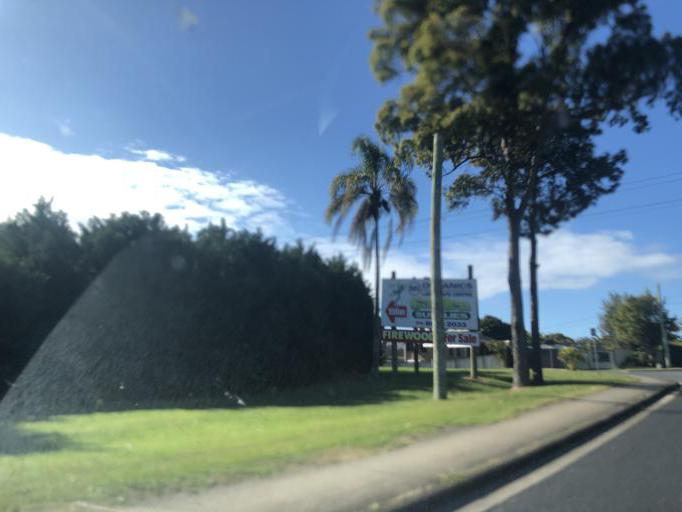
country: AU
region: New South Wales
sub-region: Coffs Harbour
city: Boambee
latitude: -30.3385
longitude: 153.0825
